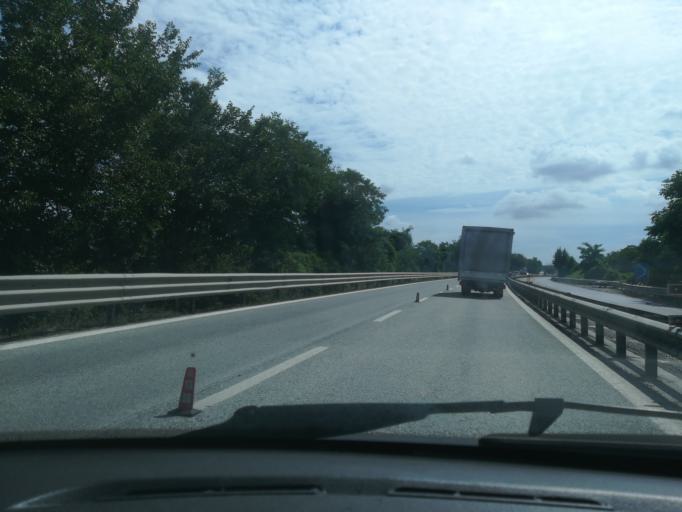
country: IT
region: The Marches
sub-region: Provincia di Macerata
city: Zona Industriale
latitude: 43.2692
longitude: 13.5015
